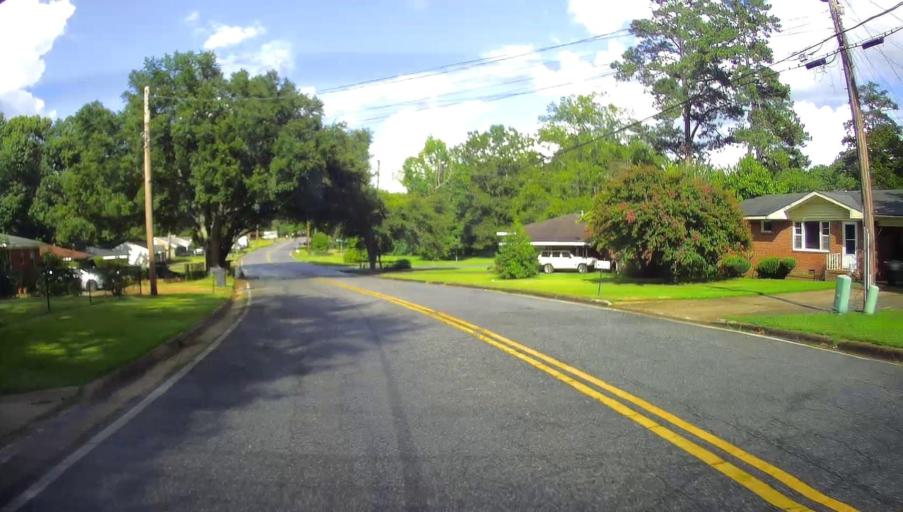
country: US
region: Alabama
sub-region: Russell County
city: Phenix City
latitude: 32.5209
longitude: -84.9814
